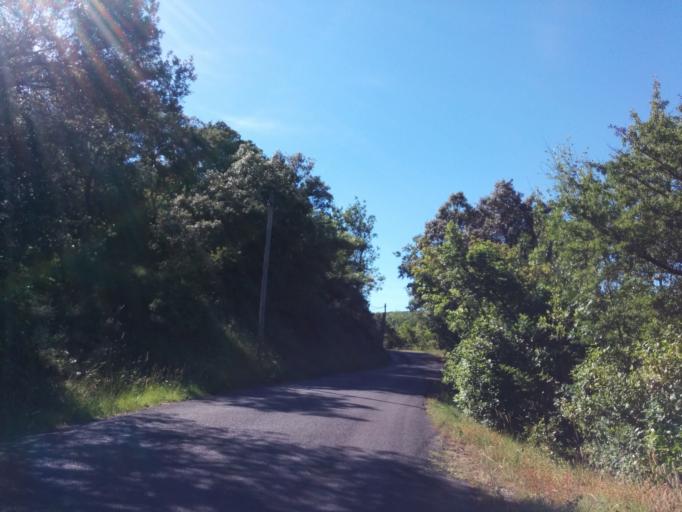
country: FR
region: Languedoc-Roussillon
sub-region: Departement du Gard
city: Saint-Christol-les-Ales
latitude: 44.0966
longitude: 4.0644
